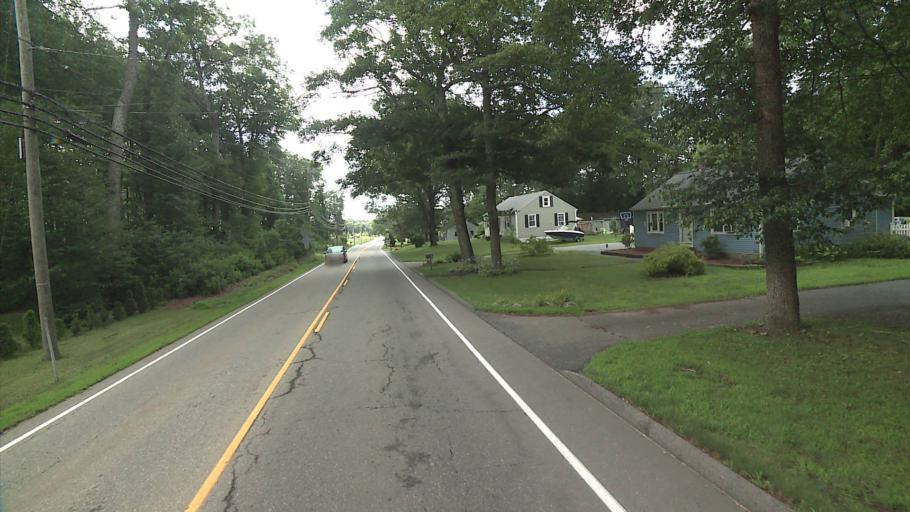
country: US
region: Connecticut
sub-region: Middlesex County
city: Clinton
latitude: 41.3037
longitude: -72.5339
